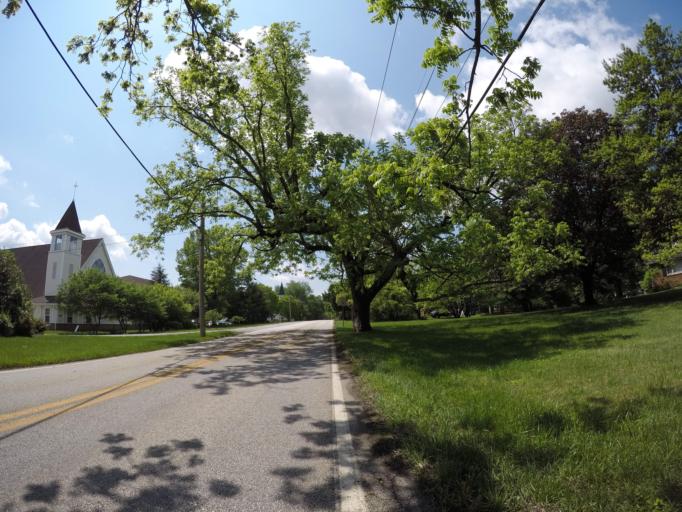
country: US
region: Maryland
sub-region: Howard County
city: Columbia
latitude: 39.2934
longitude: -76.8565
